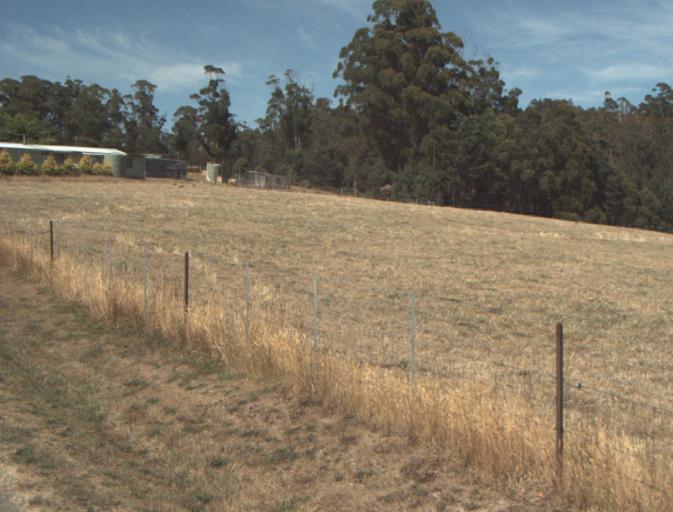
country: AU
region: Tasmania
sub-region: Launceston
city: Mayfield
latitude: -41.2347
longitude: 147.2557
